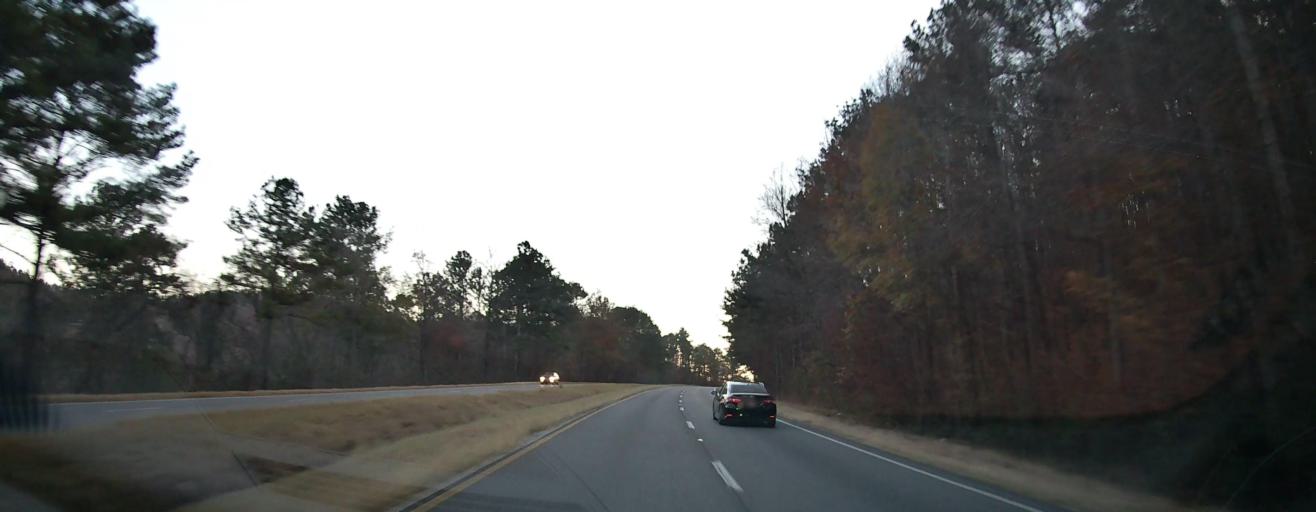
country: US
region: Alabama
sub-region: Etowah County
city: Glencoe
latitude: 33.9390
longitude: -85.9147
